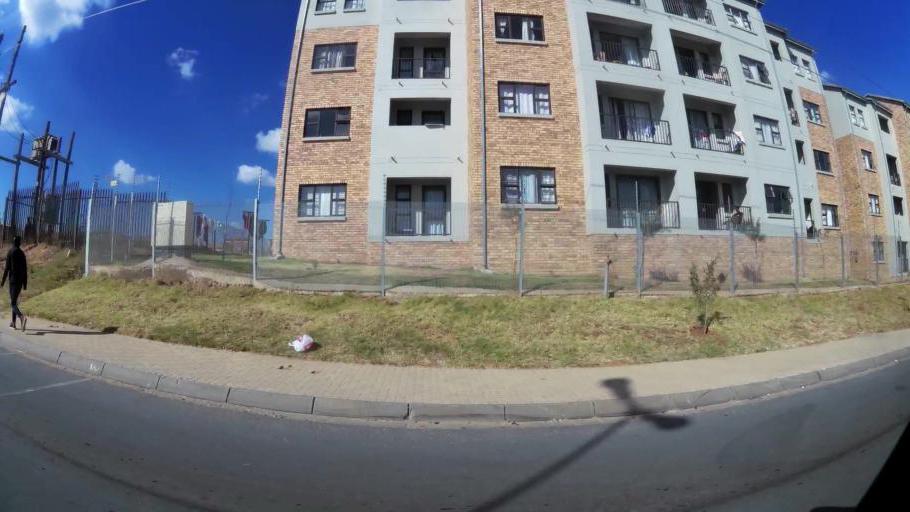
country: ZA
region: Gauteng
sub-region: West Rand District Municipality
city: Muldersdriseloop
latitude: -26.0372
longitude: 27.9194
